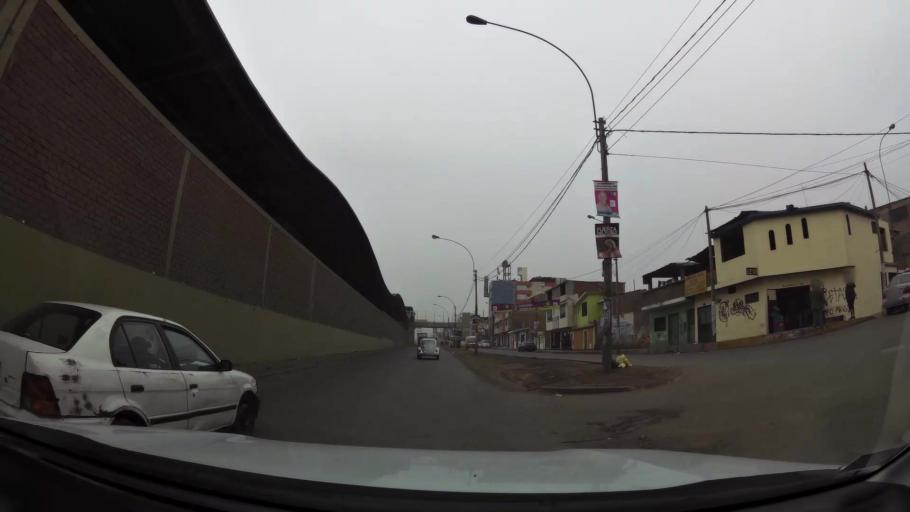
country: PE
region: Lima
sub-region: Lima
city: Surco
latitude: -12.1695
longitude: -76.9500
